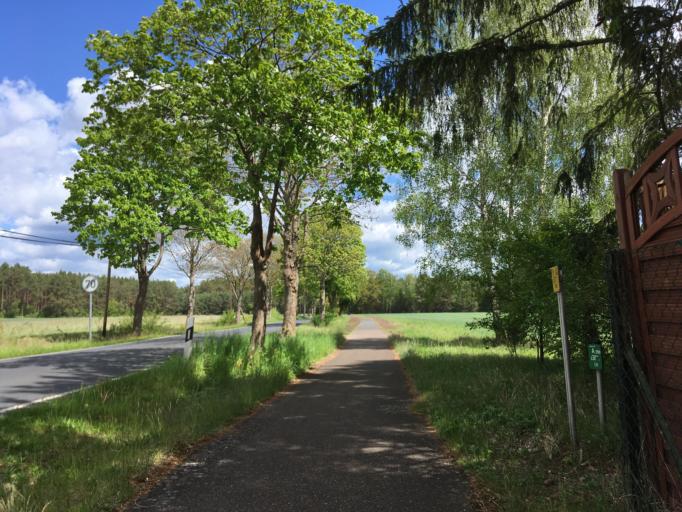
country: DE
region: Brandenburg
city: Liebenwalde
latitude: 52.8926
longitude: 13.4971
